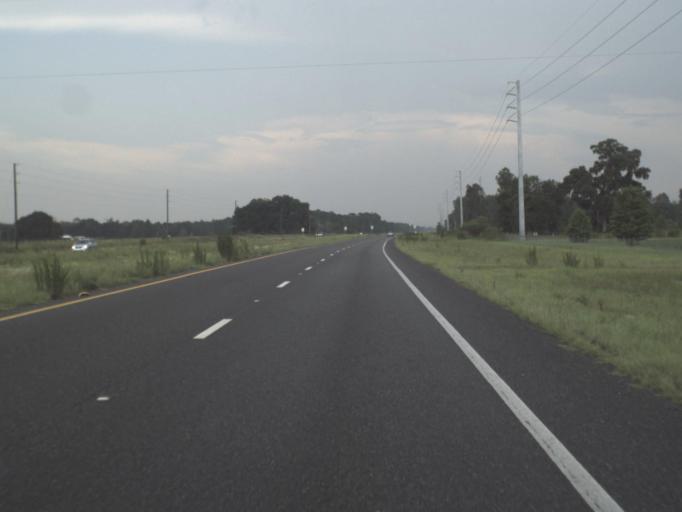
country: US
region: Florida
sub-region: Levy County
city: Bronson
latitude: 29.4754
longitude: -82.7346
